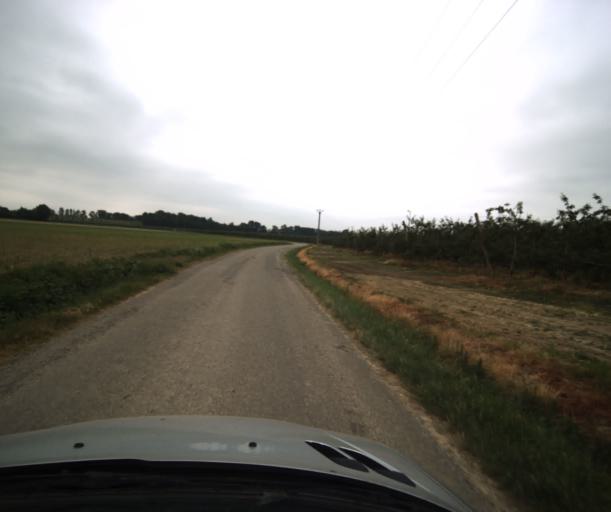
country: FR
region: Midi-Pyrenees
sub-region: Departement du Tarn-et-Garonne
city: Saint-Nicolas-de-la-Grave
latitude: 44.0683
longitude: 0.9864
